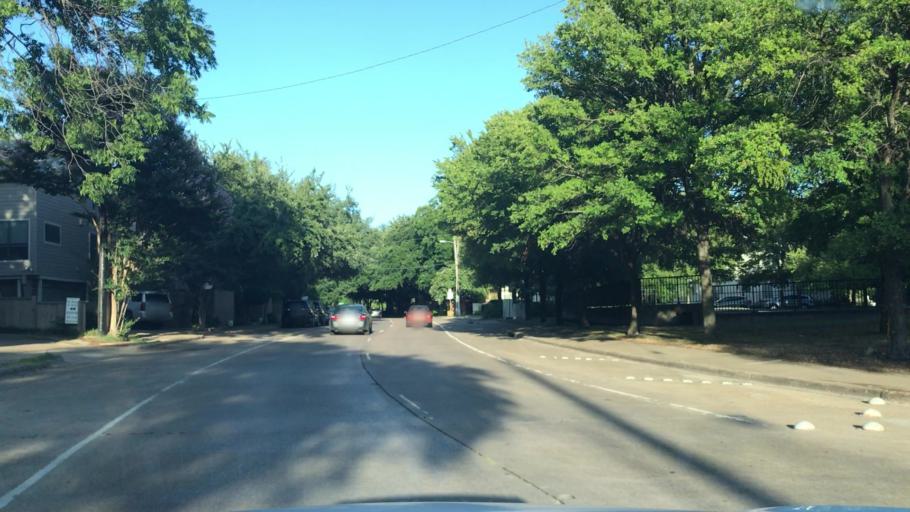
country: US
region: Texas
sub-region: Dallas County
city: Highland Park
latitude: 32.8179
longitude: -96.8069
